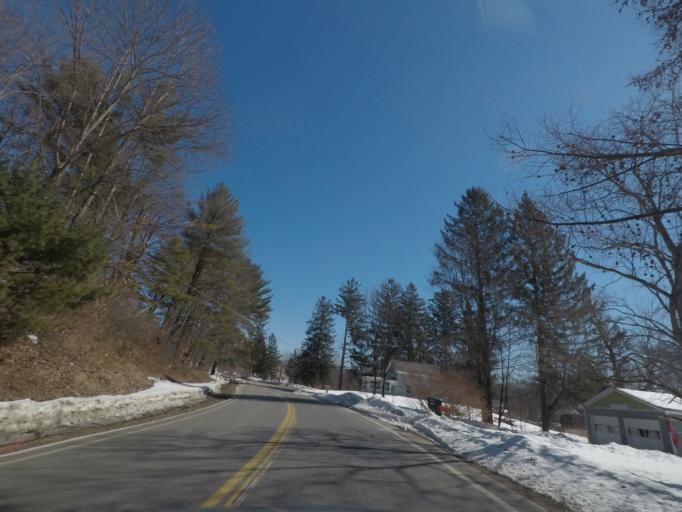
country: US
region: New York
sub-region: Saratoga County
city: Schuylerville
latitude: 43.1196
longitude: -73.5695
